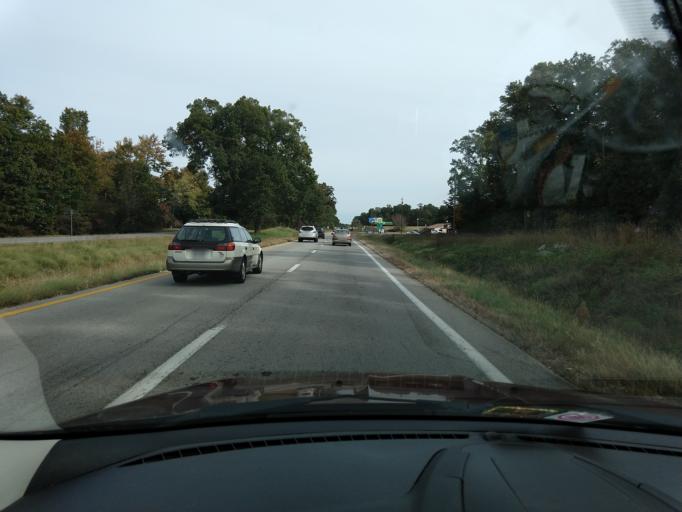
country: US
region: Virginia
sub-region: Pittsylvania County
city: Chatham
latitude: 36.8948
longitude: -79.3972
